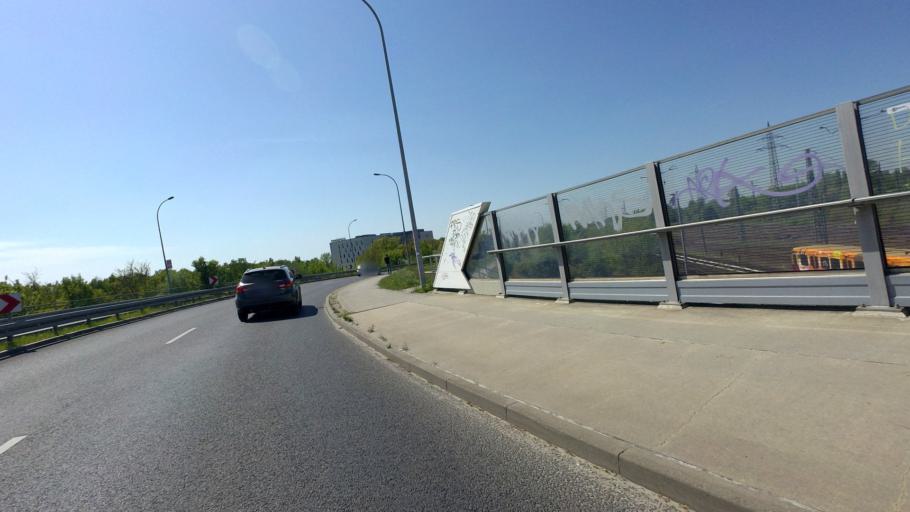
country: DE
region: Brandenburg
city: Schonefeld
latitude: 52.3943
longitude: 13.5202
